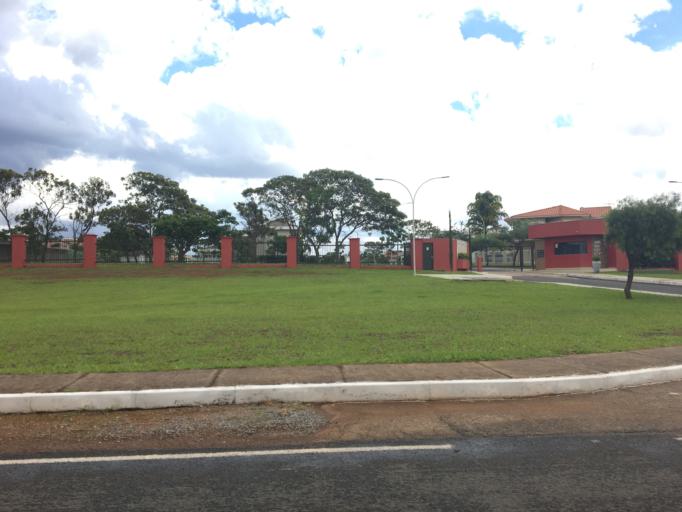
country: BR
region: Federal District
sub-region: Brasilia
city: Brasilia
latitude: -15.8946
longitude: -47.9124
